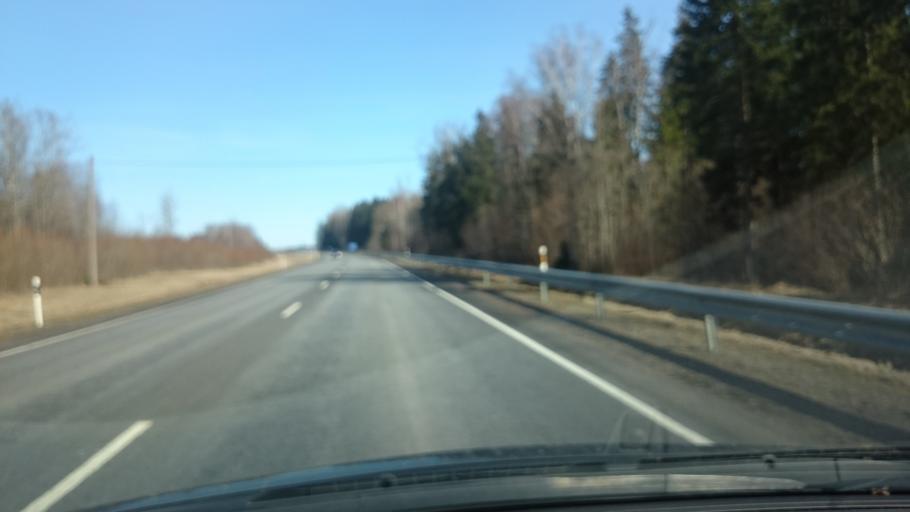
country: EE
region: Paernumaa
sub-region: Vaendra vald (alev)
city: Vandra
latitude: 58.6488
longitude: 24.9904
